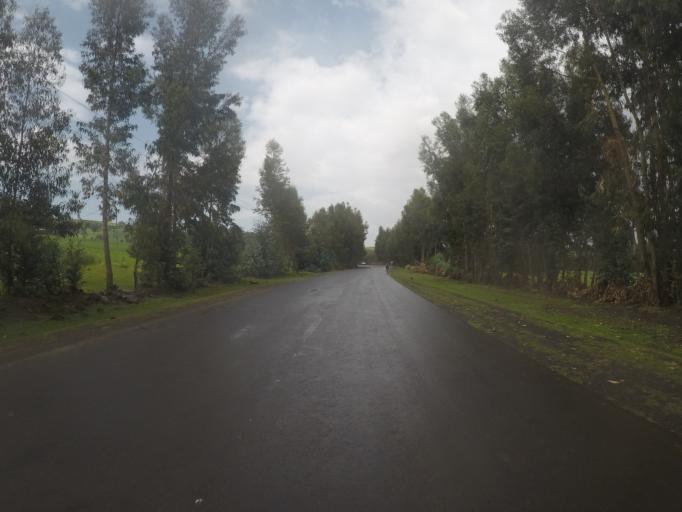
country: ET
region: Amhara
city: Debark'
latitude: 13.1137
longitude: 37.8688
